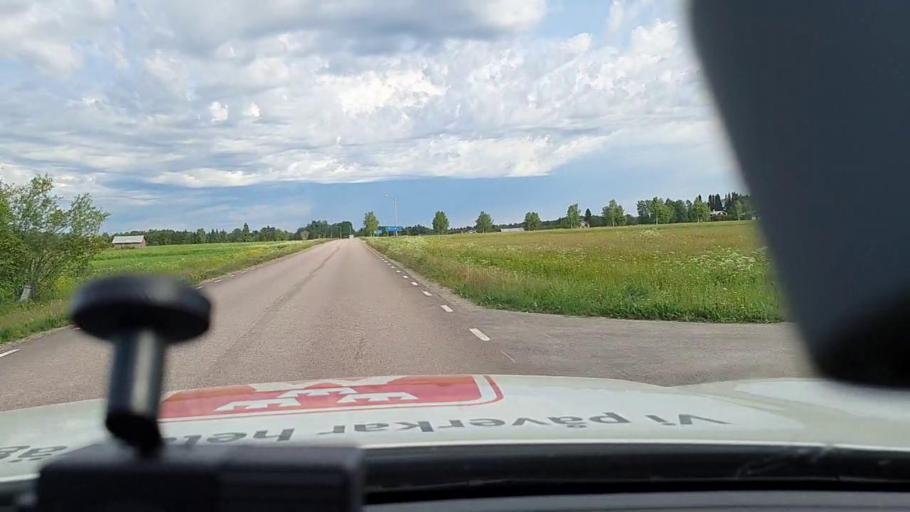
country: SE
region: Norrbotten
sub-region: Bodens Kommun
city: Saevast
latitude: 65.6919
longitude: 21.7832
